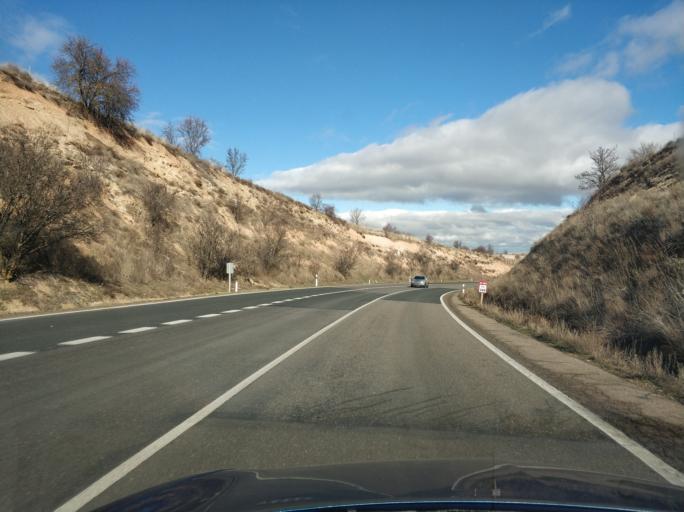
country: ES
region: Castille and Leon
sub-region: Provincia de Burgos
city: Fuentecen
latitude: 41.6313
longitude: -3.8724
